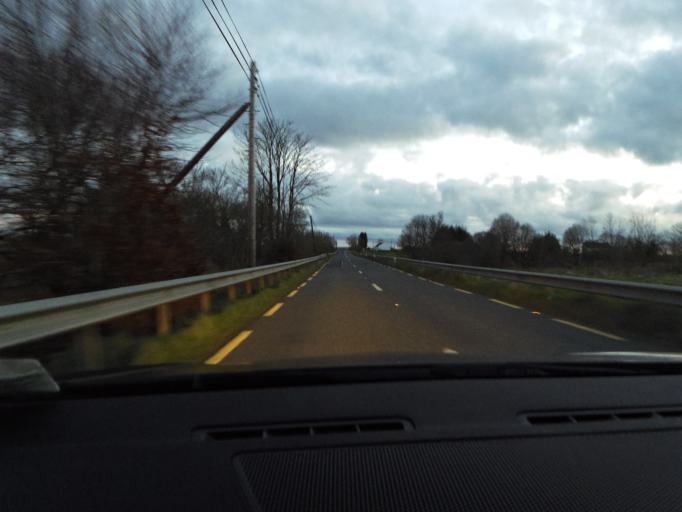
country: IE
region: Connaught
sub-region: Roscommon
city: Roscommon
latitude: 53.7947
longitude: -8.2394
